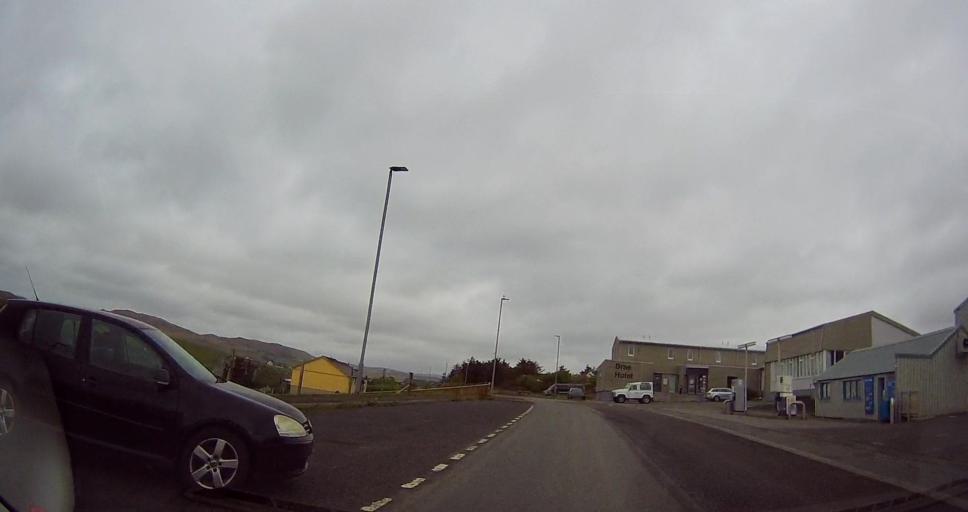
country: GB
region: Scotland
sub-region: Shetland Islands
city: Lerwick
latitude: 60.3909
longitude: -1.3490
